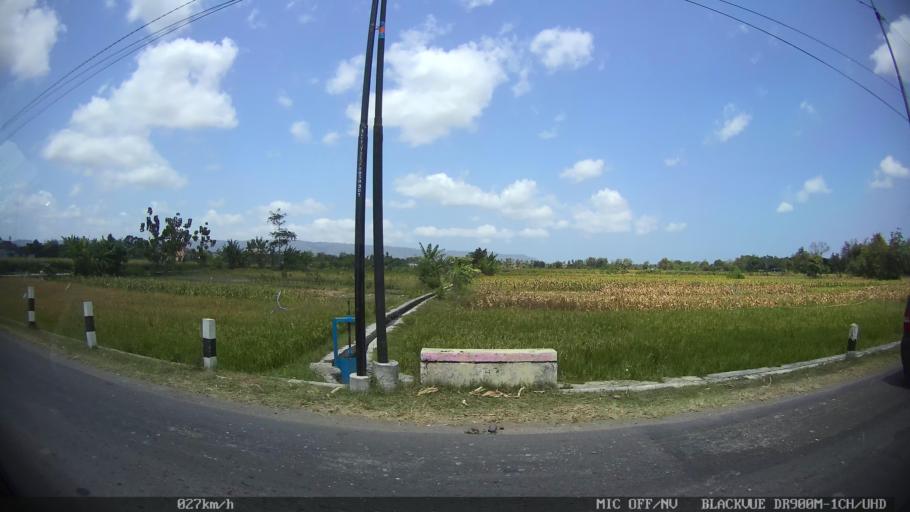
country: ID
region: Daerah Istimewa Yogyakarta
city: Bantul
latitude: -7.9094
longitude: 110.3500
